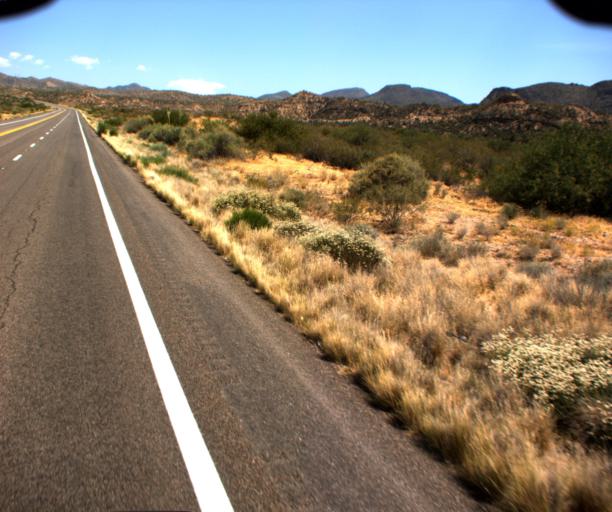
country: US
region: Arizona
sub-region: Gila County
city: Miami
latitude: 33.5916
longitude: -110.9874
